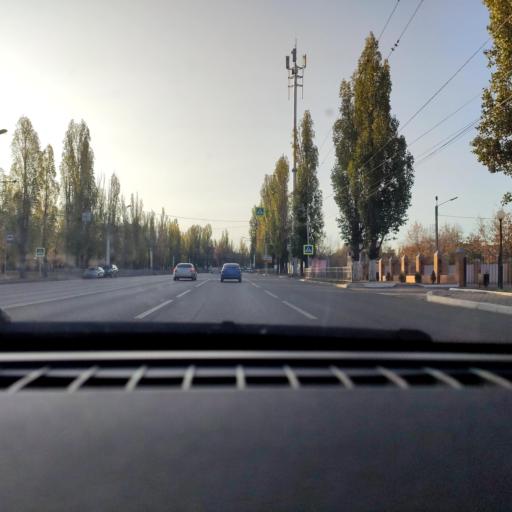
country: RU
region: Voronezj
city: Maslovka
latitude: 51.6195
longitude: 39.2364
